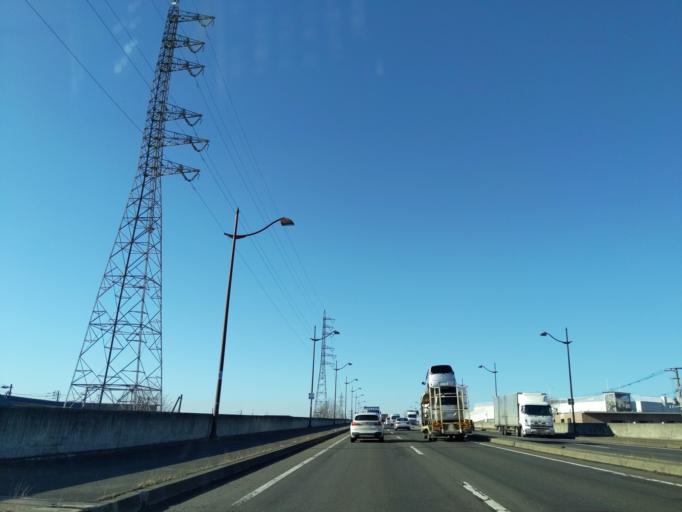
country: JP
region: Hokkaido
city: Kitahiroshima
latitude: 42.8997
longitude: 141.5768
